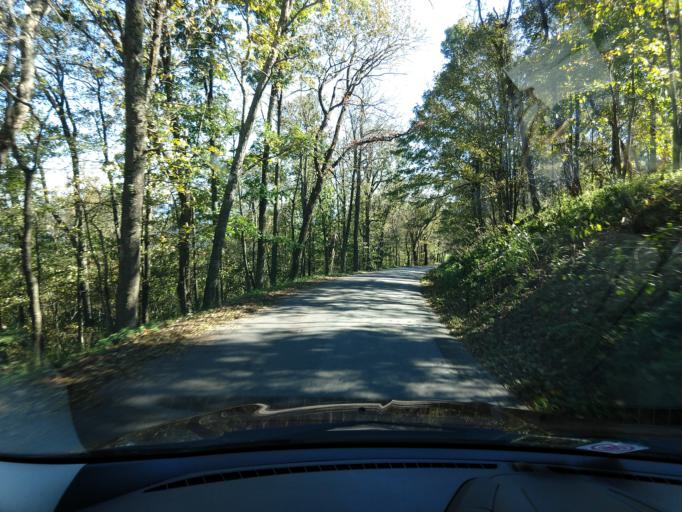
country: US
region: Virginia
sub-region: Alleghany County
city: Clifton Forge
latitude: 37.8737
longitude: -79.8870
